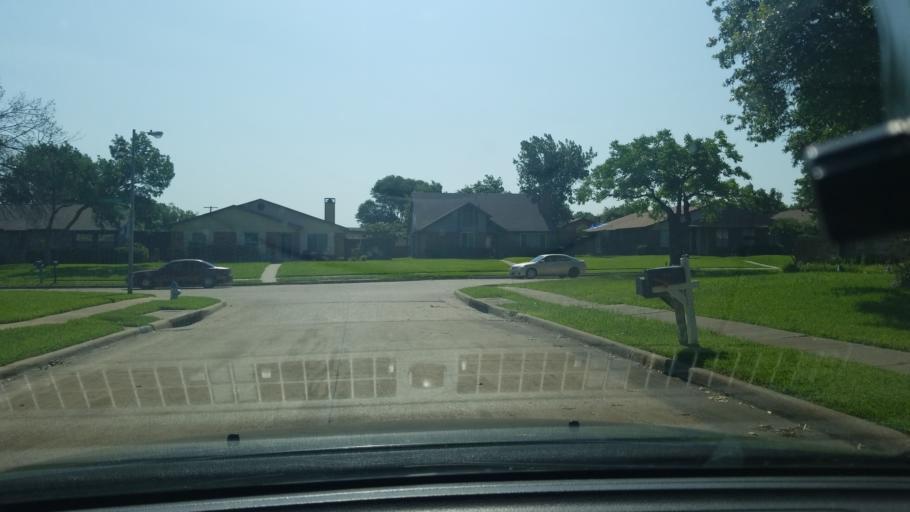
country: US
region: Texas
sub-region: Dallas County
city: Mesquite
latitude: 32.8182
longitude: -96.6185
